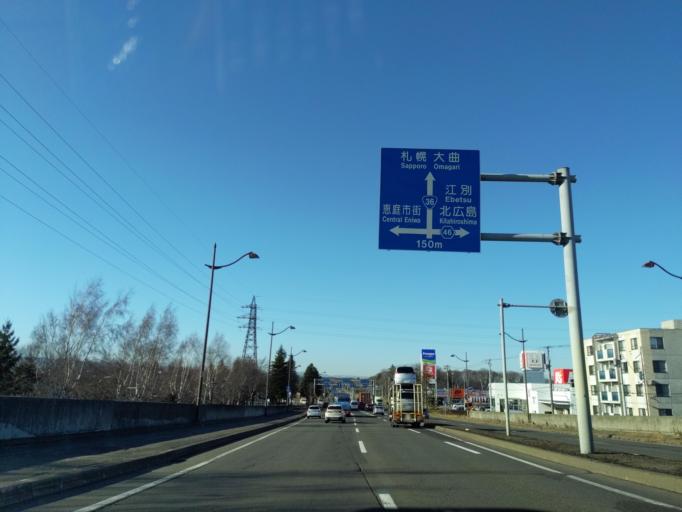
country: JP
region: Hokkaido
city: Kitahiroshima
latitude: 42.9013
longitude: 141.5725
